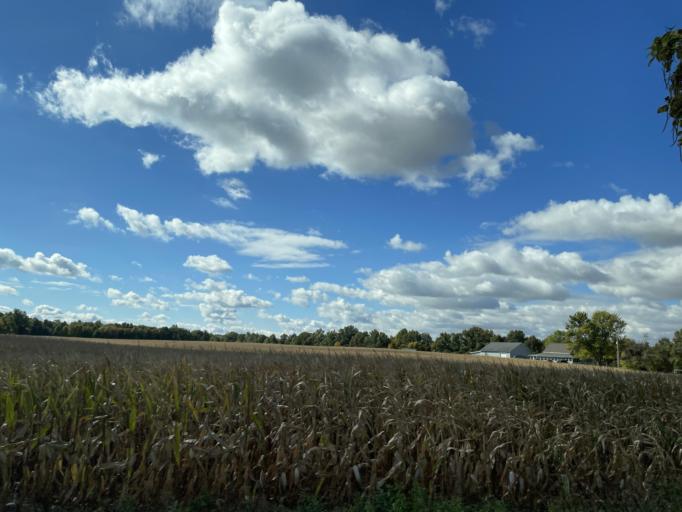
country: US
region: Indiana
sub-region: Allen County
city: Fort Wayne
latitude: 41.1181
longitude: -85.2358
